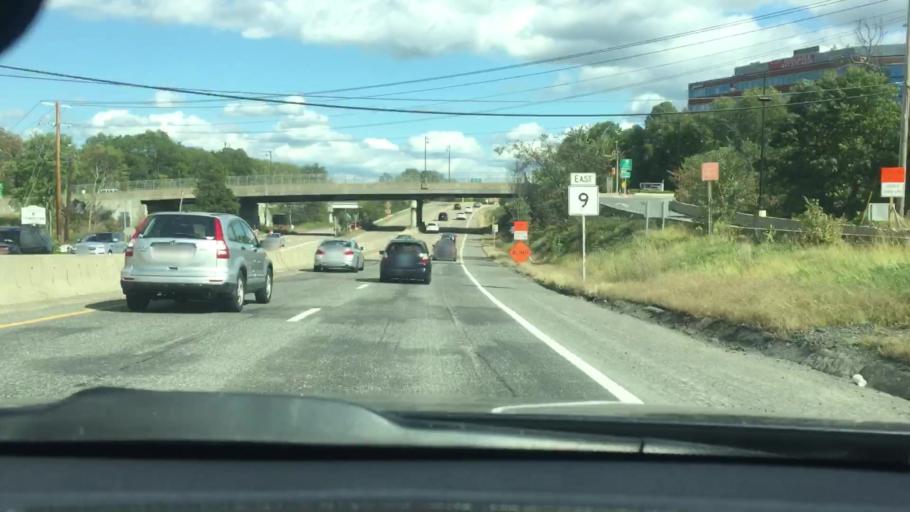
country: US
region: Massachusetts
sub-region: Worcester County
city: Southborough
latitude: 42.2941
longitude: -71.5058
